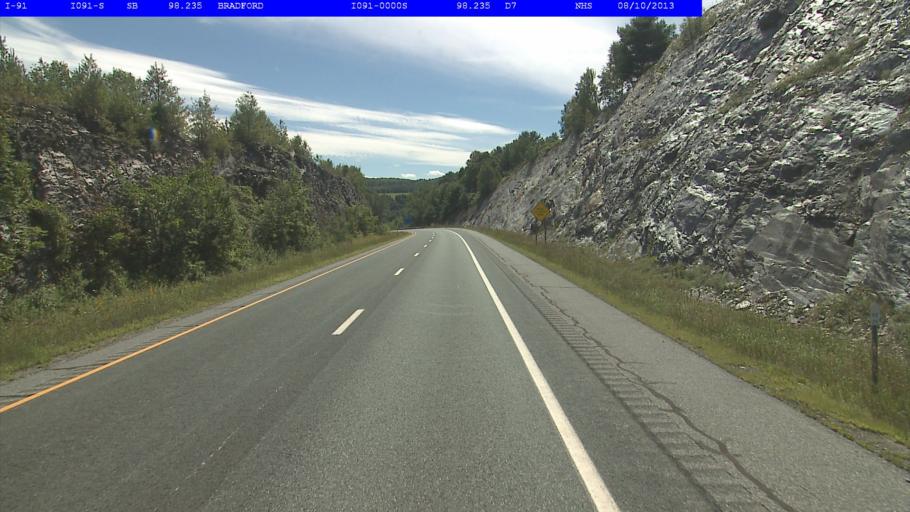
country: US
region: New Hampshire
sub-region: Grafton County
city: Haverhill
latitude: 43.9916
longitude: -72.1351
